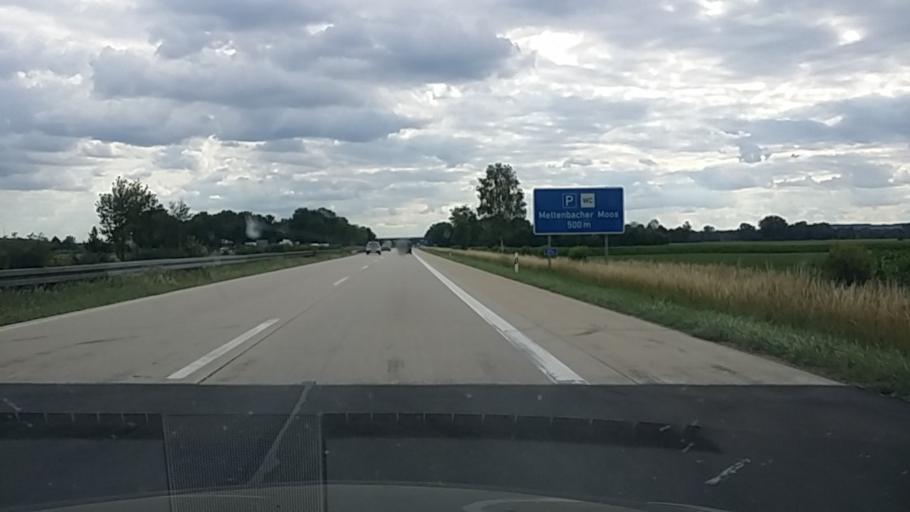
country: DE
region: Bavaria
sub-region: Lower Bavaria
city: Niederaichbach
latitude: 48.6199
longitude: 12.2965
